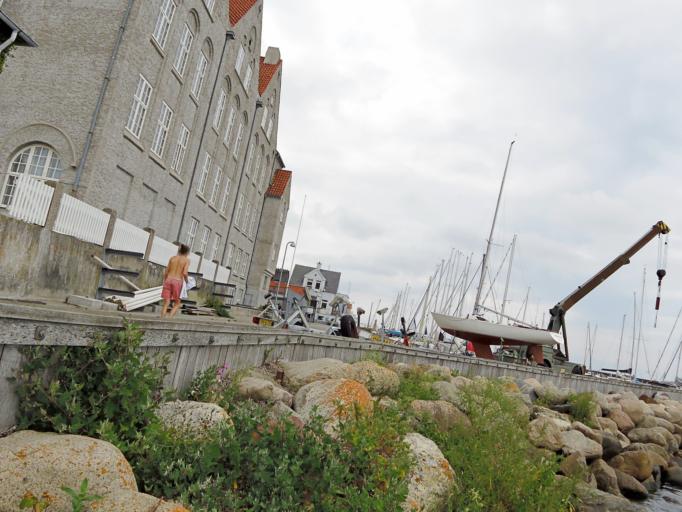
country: DK
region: Capital Region
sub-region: Gentofte Kommune
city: Charlottenlund
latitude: 55.7867
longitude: 12.5954
